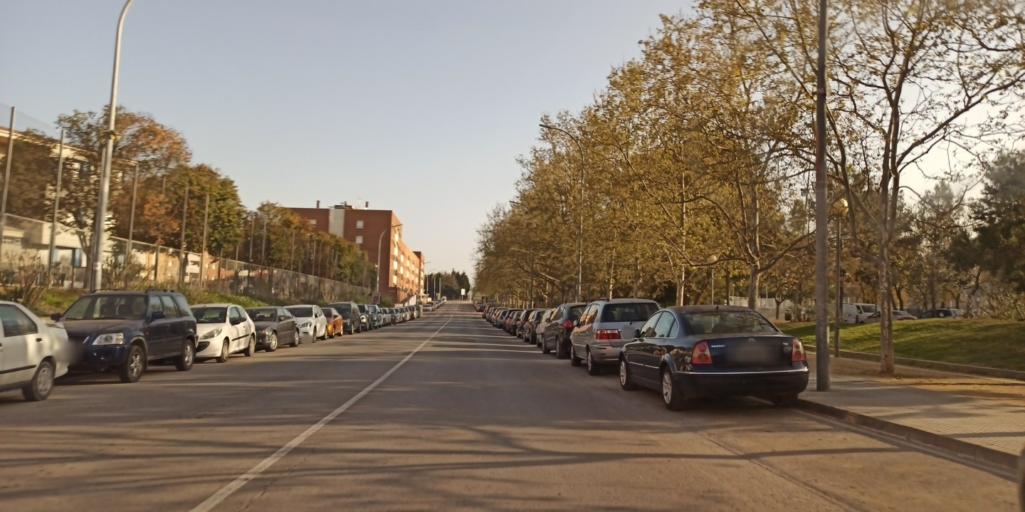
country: ES
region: Catalonia
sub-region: Provincia de Barcelona
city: Vilafranca del Penedes
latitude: 41.3514
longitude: 1.7058
